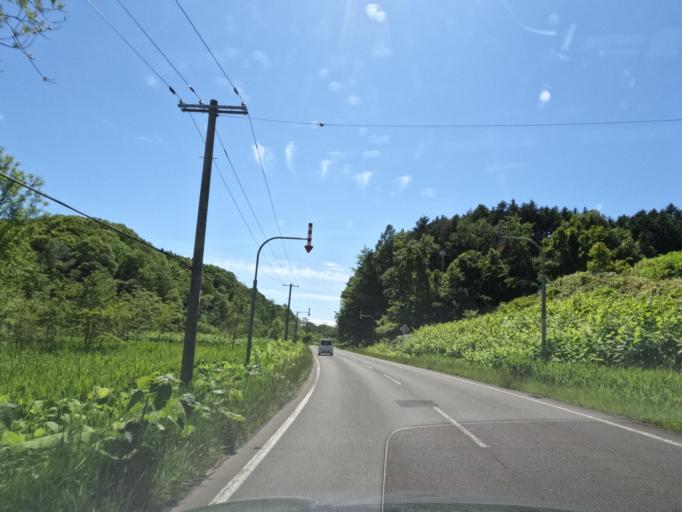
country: JP
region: Hokkaido
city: Iwamizawa
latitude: 43.1004
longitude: 141.7714
